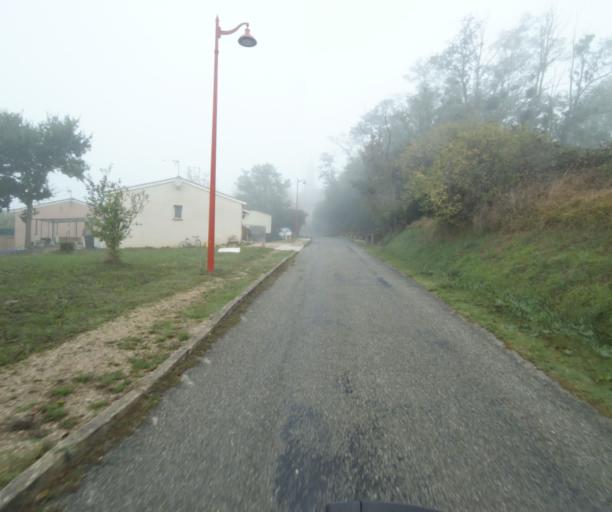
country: FR
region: Midi-Pyrenees
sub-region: Departement du Tarn-et-Garonne
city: Nohic
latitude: 43.9223
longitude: 1.4708
